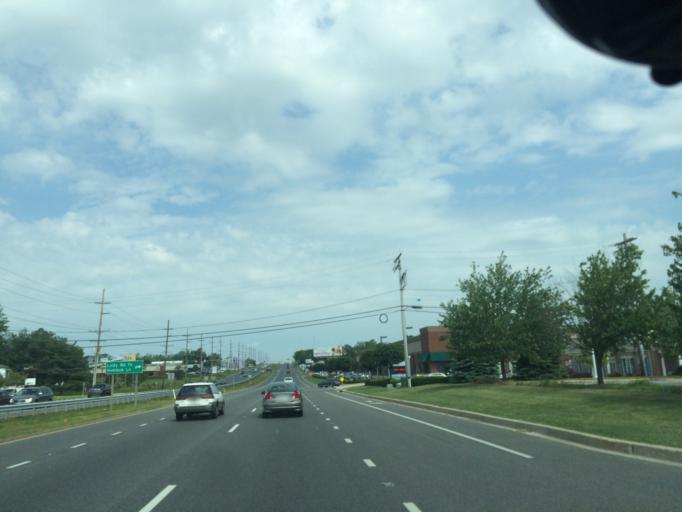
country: US
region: Maryland
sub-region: Carroll County
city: Westminster
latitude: 39.5545
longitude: -76.9577
